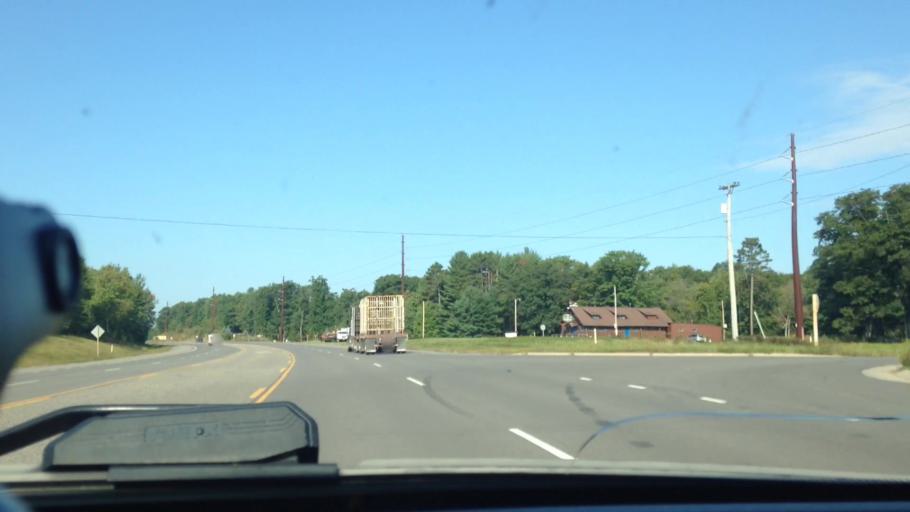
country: US
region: Michigan
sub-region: Dickinson County
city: Iron Mountain
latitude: 45.8817
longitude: -88.1294
